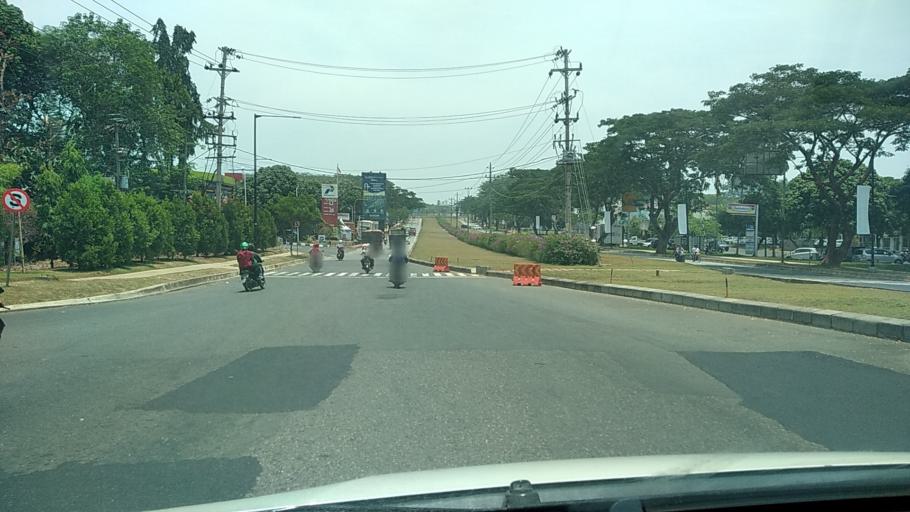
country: ID
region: Central Java
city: Semarang
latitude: -7.0271
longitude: 110.3348
